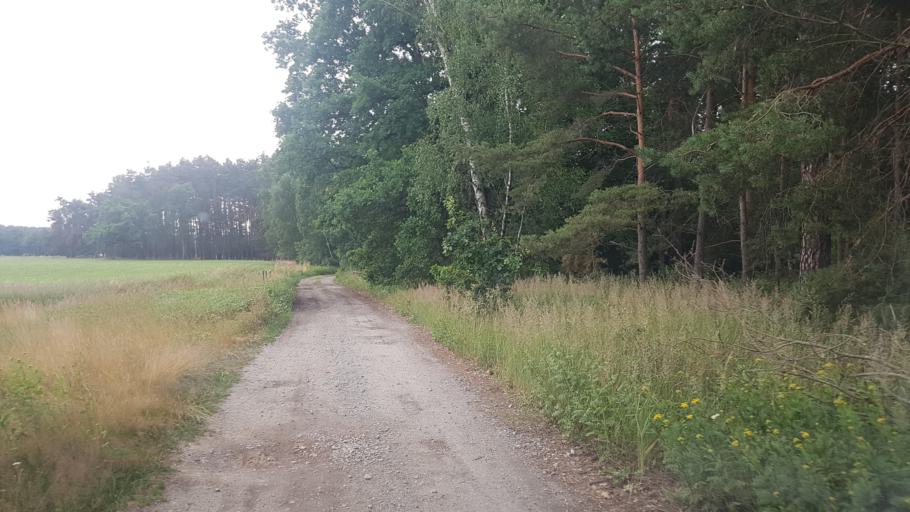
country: DE
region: Brandenburg
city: Crinitz
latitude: 51.7218
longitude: 13.8251
